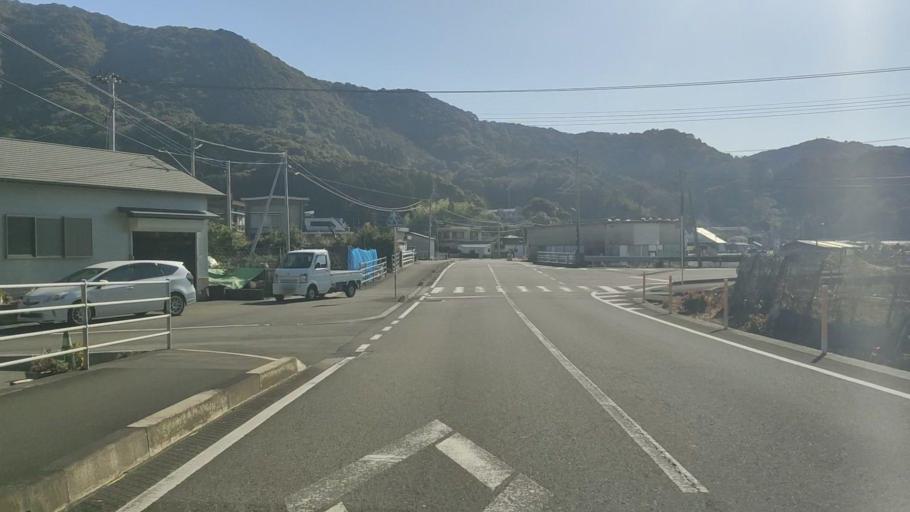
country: JP
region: Oita
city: Saiki
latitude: 32.8033
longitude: 131.8989
